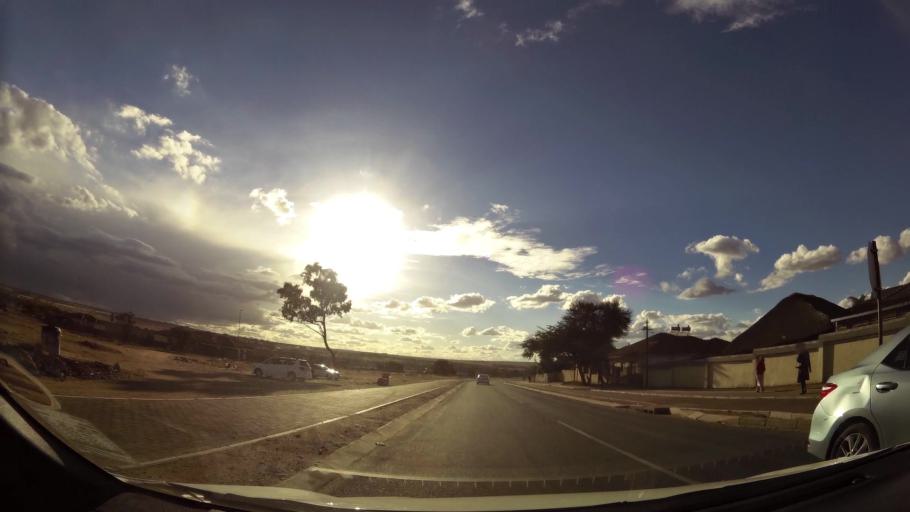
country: ZA
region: Limpopo
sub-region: Capricorn District Municipality
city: Polokwane
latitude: -23.9172
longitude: 29.4284
